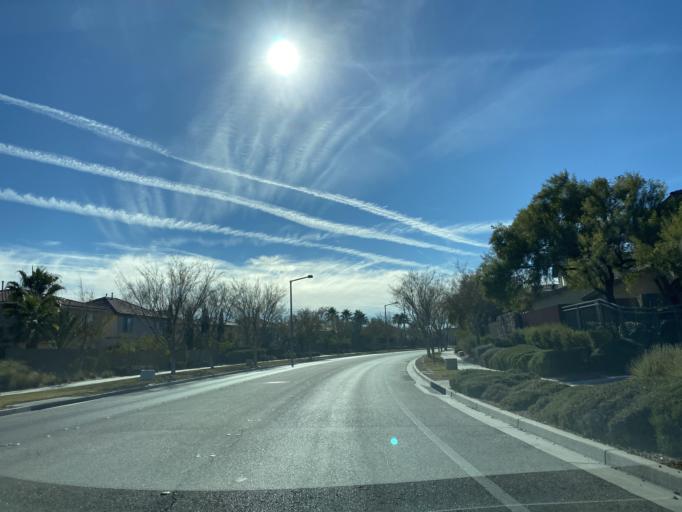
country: US
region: Nevada
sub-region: Clark County
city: Summerlin South
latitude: 36.1489
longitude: -115.3183
